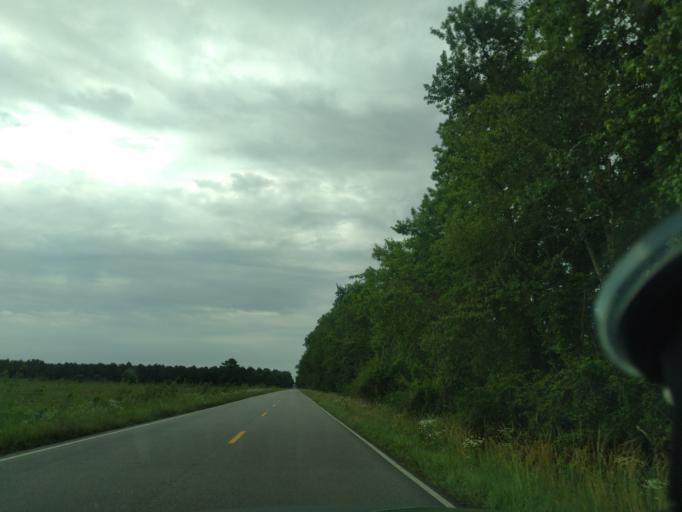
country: US
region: North Carolina
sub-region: Washington County
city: Plymouth
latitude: 35.8608
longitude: -76.5786
